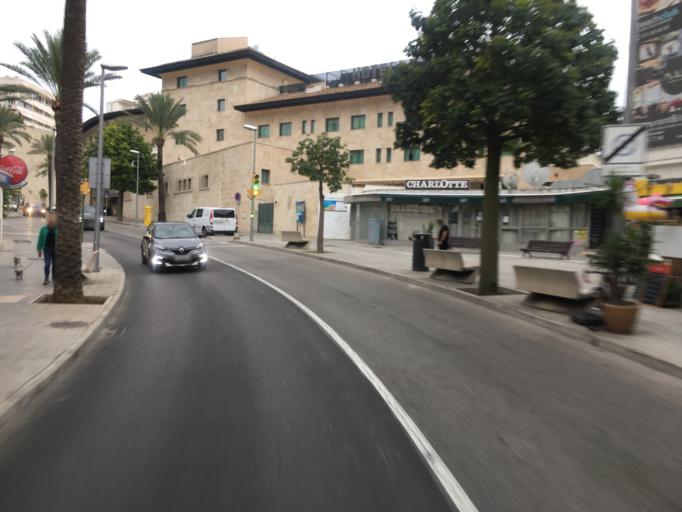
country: ES
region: Balearic Islands
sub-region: Illes Balears
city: Palma
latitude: 39.5529
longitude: 2.6068
